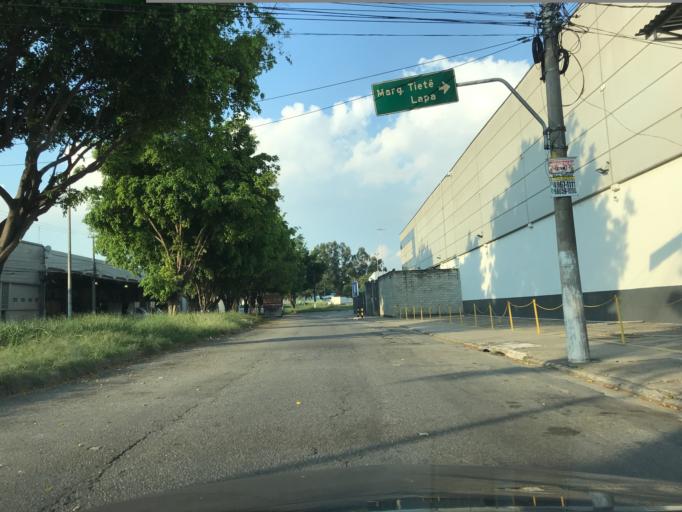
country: BR
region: Sao Paulo
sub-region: Osasco
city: Osasco
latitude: -23.5240
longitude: -46.7423
